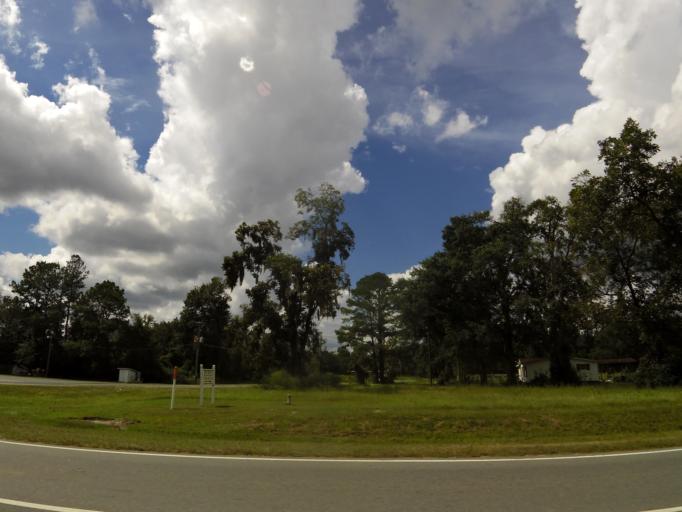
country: US
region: Georgia
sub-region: Brantley County
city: Nahunta
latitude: 31.1493
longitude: -81.9915
